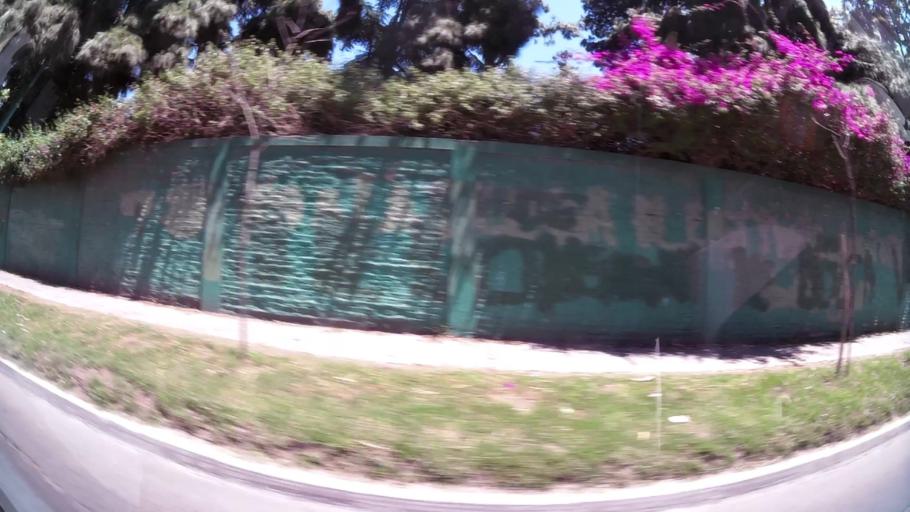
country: AR
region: Buenos Aires
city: Hurlingham
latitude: -34.5084
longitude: -58.6831
